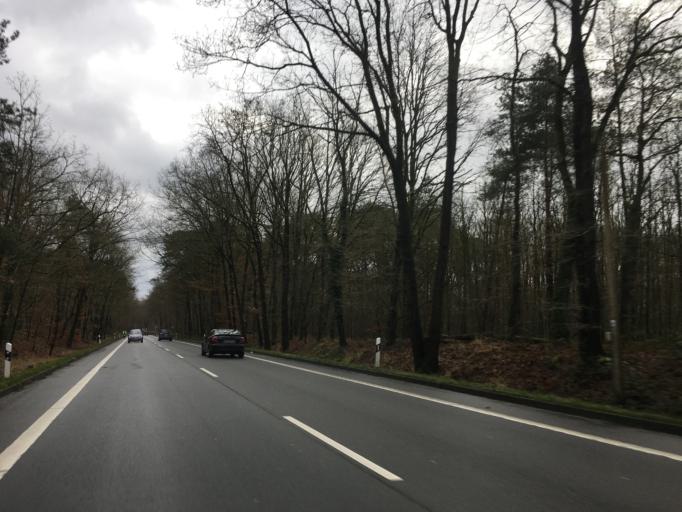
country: DE
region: North Rhine-Westphalia
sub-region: Regierungsbezirk Munster
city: Haltern
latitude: 51.7527
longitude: 7.2416
